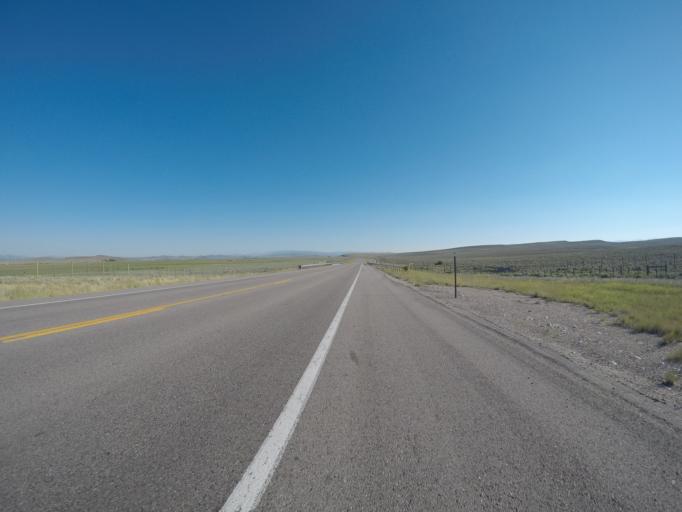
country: US
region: Wyoming
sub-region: Sublette County
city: Pinedale
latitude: 42.9243
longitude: -110.0807
